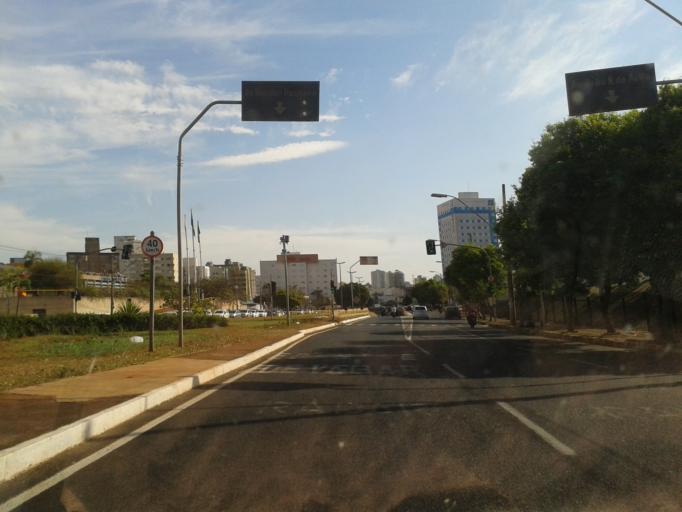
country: BR
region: Minas Gerais
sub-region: Uberlandia
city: Uberlandia
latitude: -18.9116
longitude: -48.2569
